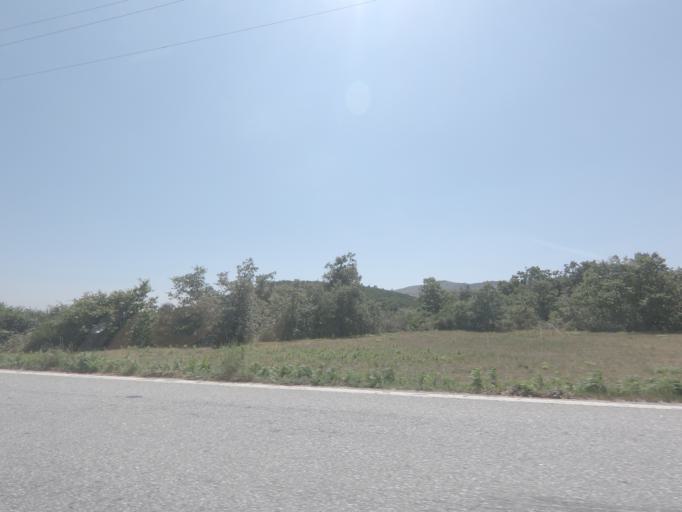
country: PT
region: Viseu
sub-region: Tarouca
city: Tarouca
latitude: 40.9971
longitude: -7.8847
